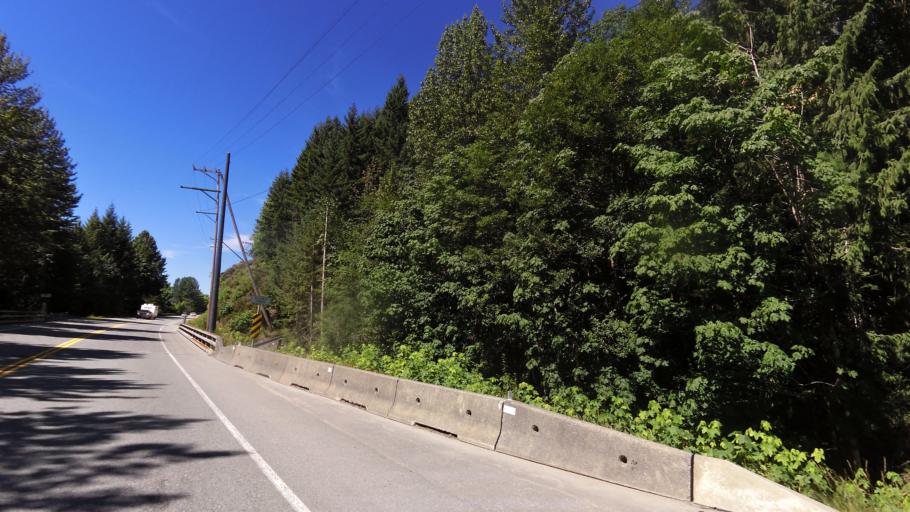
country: CA
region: British Columbia
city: Port Alberni
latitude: 49.2745
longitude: -125.0476
